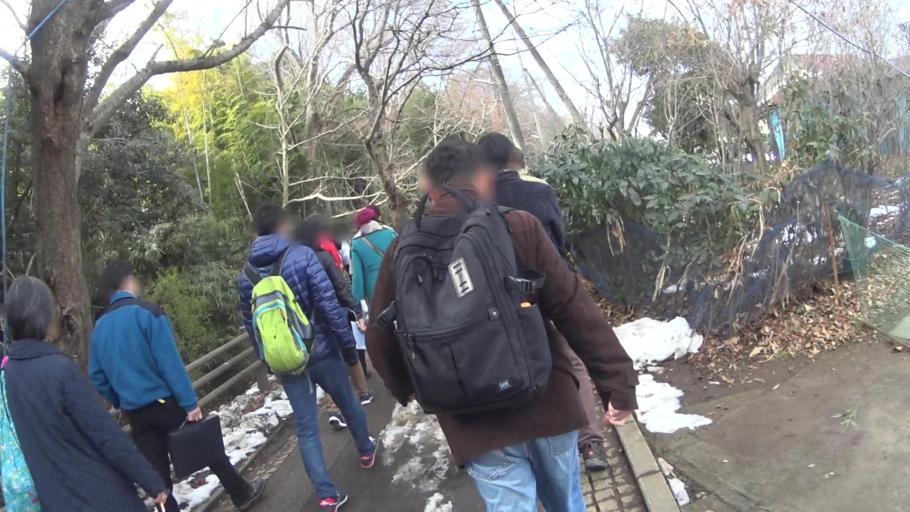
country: JP
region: Saitama
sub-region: Kawaguchi-shi
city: Hatogaya-honcho
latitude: 35.8624
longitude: 139.7100
